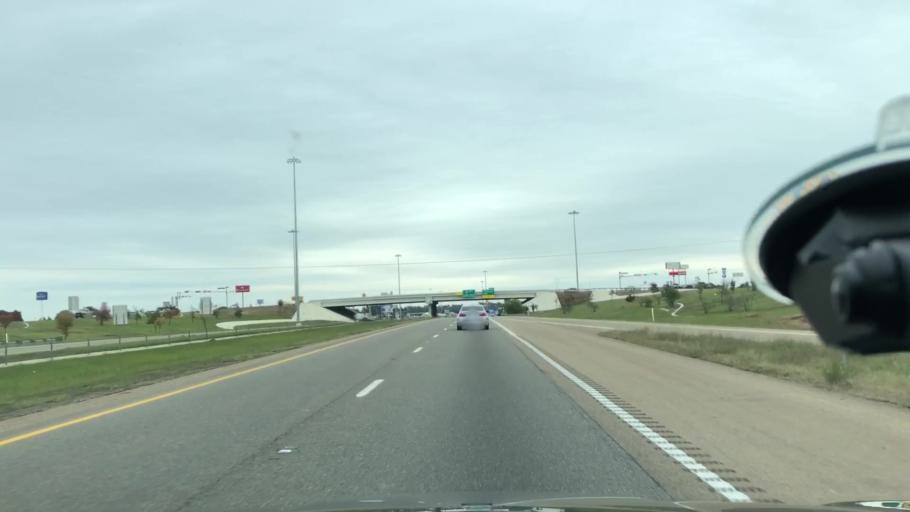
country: US
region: Arkansas
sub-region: Miller County
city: Texarkana
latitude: 33.4701
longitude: -94.0464
